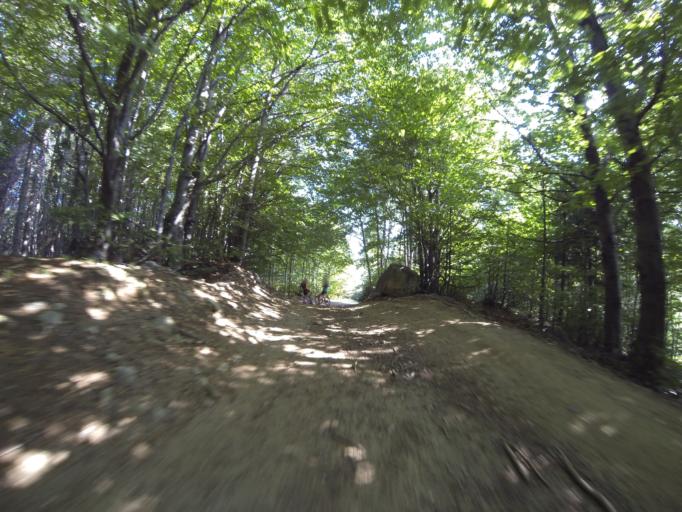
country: RO
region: Valcea
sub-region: Comuna Vaideeni
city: Vaideeni
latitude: 45.2329
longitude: 23.9631
